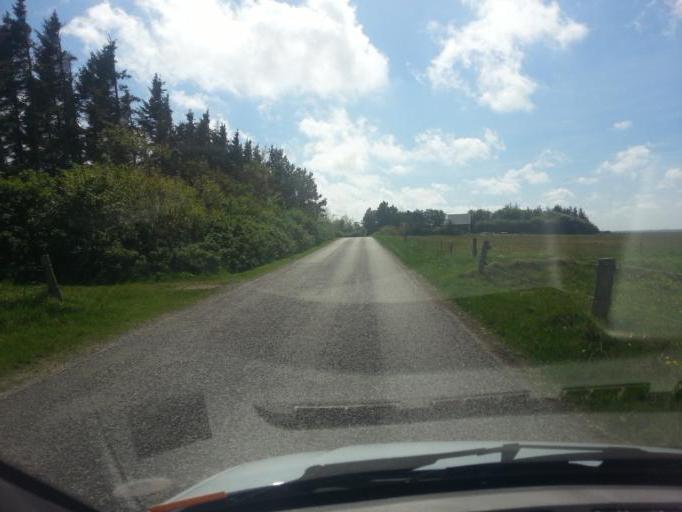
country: DK
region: South Denmark
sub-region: Varde Kommune
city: Oksbol
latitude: 55.5780
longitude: 8.3240
